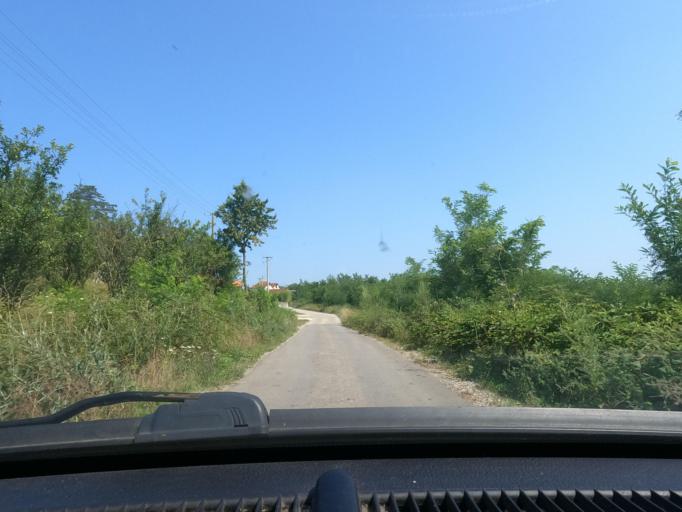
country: RS
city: Jarebice
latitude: 44.5429
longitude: 19.3761
